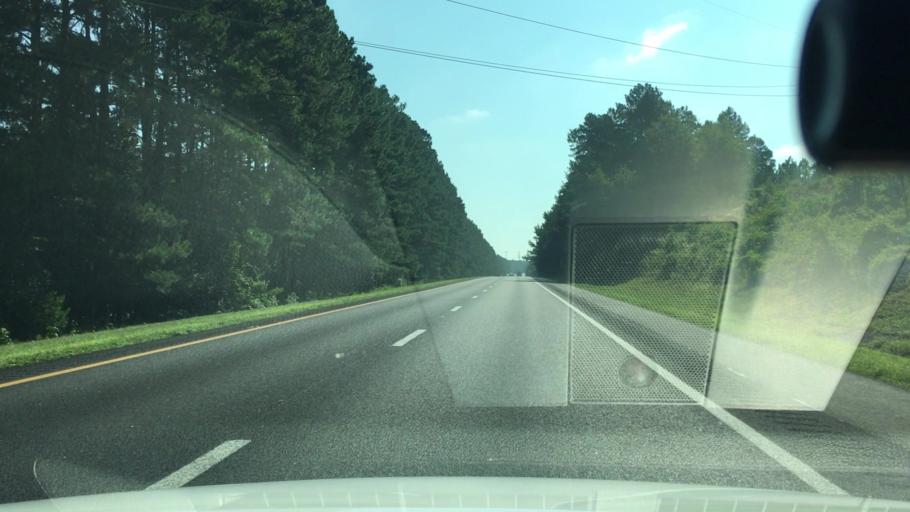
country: US
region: South Carolina
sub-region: Aiken County
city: Graniteville
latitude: 33.6293
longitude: -81.8021
